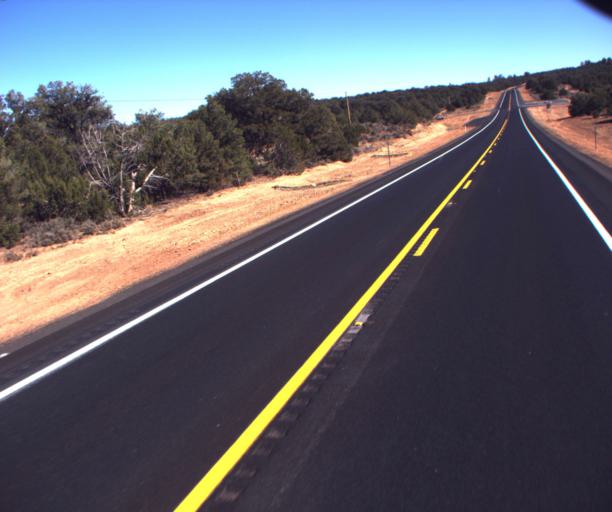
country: US
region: Arizona
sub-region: Apache County
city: Ganado
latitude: 35.7170
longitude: -109.3509
